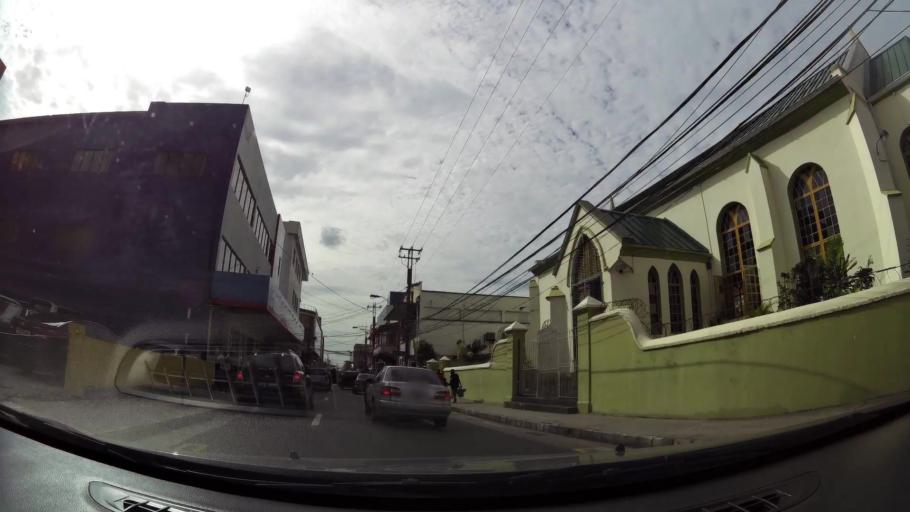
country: TT
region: San Juan/Laventille
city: Laventille
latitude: 10.6549
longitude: -61.5115
